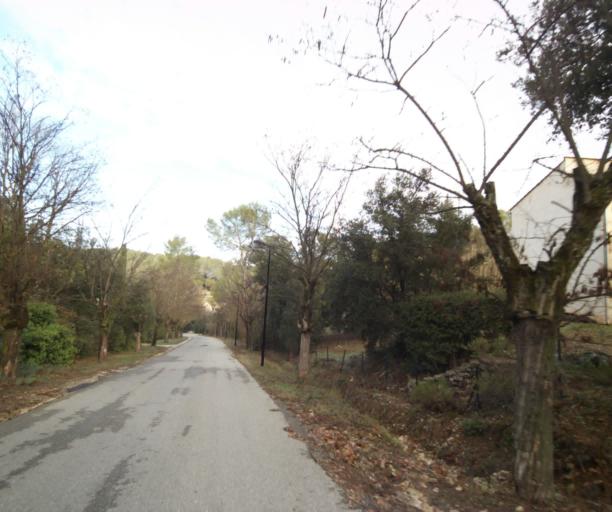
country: FR
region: Provence-Alpes-Cote d'Azur
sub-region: Departement du Var
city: Trans-en-Provence
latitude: 43.4921
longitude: 6.4931
